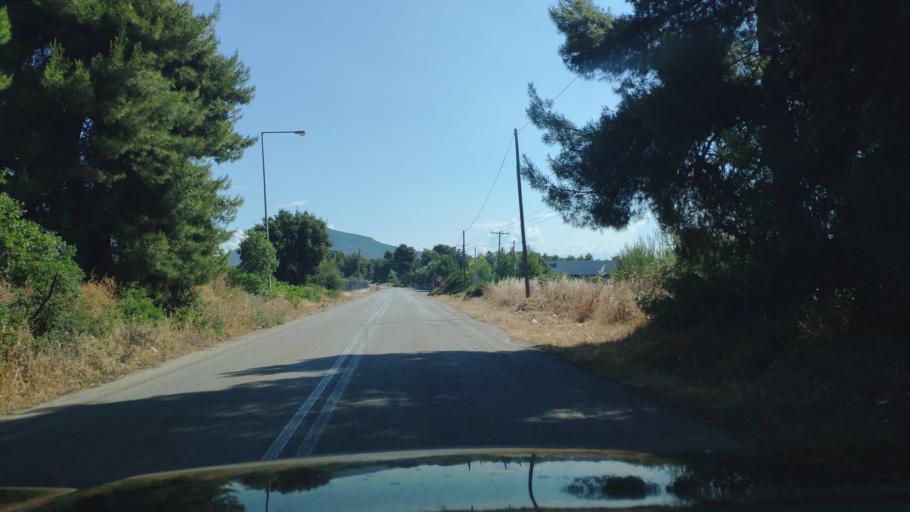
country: GR
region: Central Greece
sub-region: Nomos Voiotias
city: Arma
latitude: 38.3915
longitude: 23.5070
